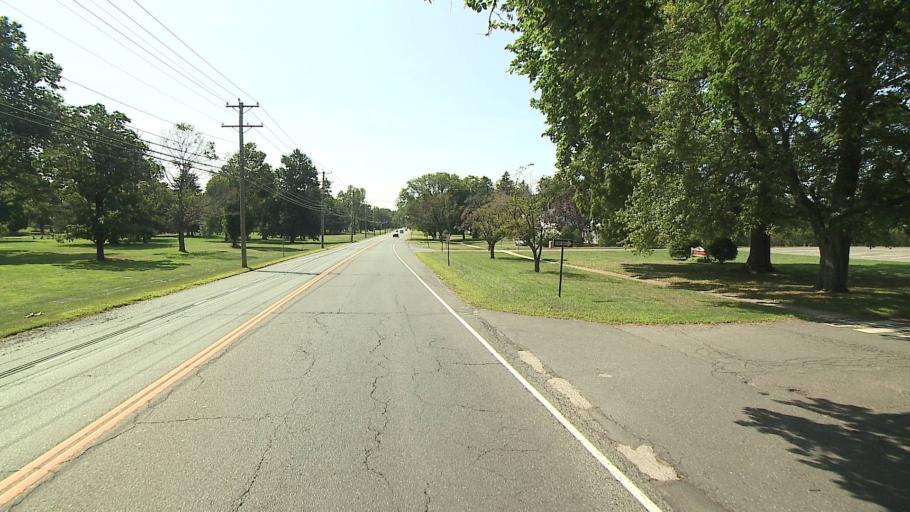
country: US
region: Connecticut
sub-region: Hartford County
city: Enfield
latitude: 41.9760
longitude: -72.5921
